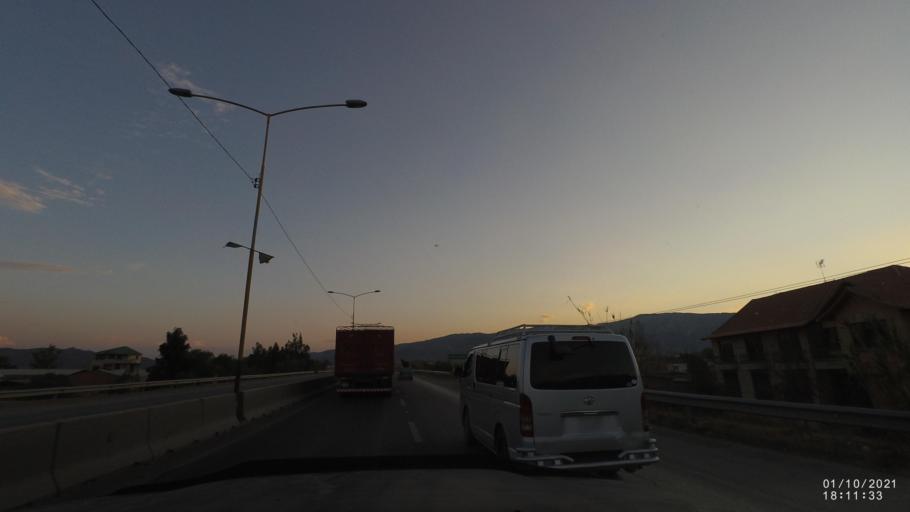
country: BO
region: Cochabamba
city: Sipe Sipe
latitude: -17.4304
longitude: -66.3322
